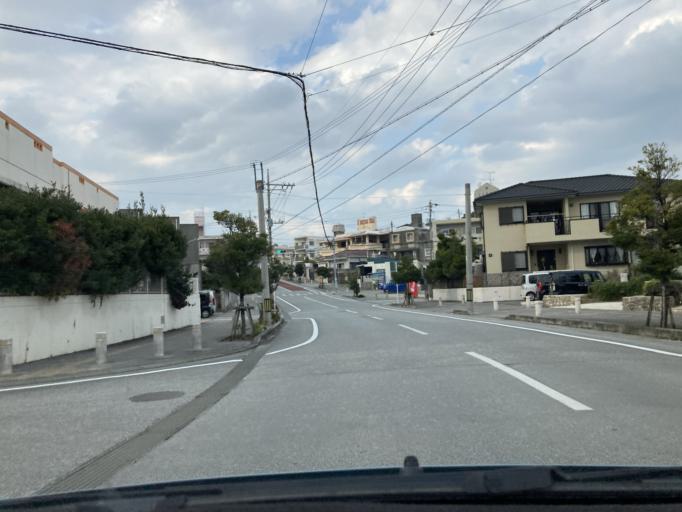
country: JP
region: Okinawa
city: Tomigusuku
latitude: 26.1952
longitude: 127.7335
